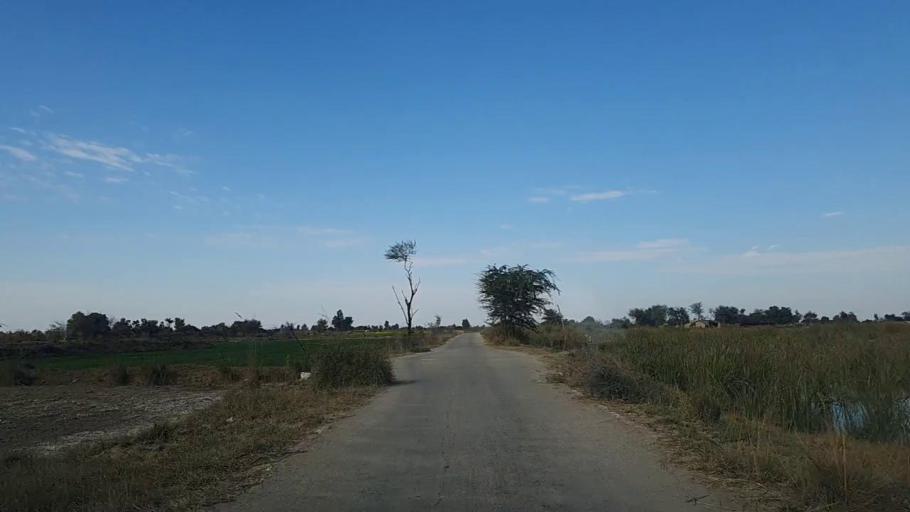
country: PK
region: Sindh
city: Khadro
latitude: 26.2844
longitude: 68.8199
